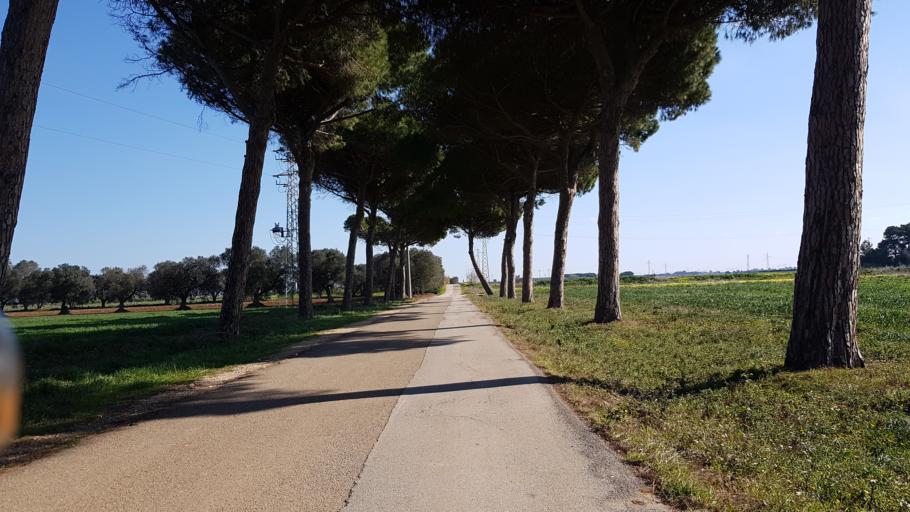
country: IT
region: Apulia
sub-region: Provincia di Brindisi
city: Mesagne
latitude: 40.6195
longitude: 17.8549
